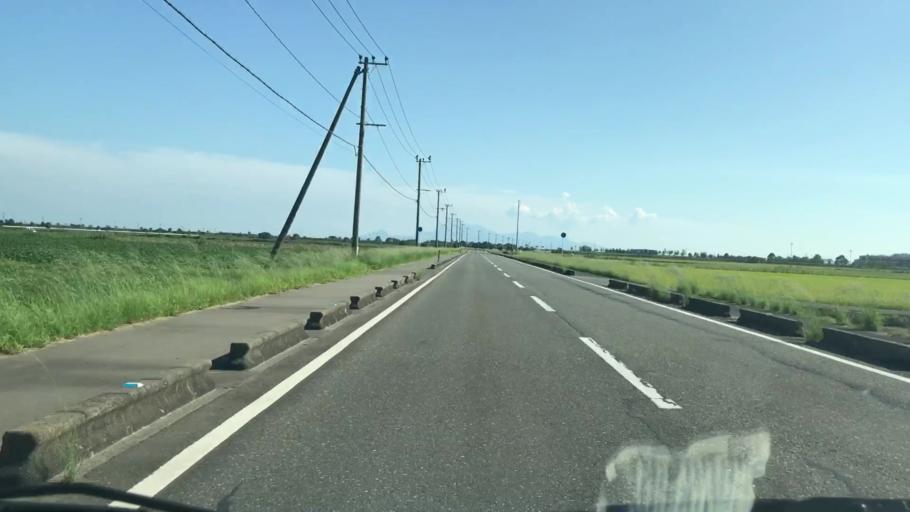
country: JP
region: Saga Prefecture
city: Okawa
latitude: 33.1622
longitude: 130.3088
